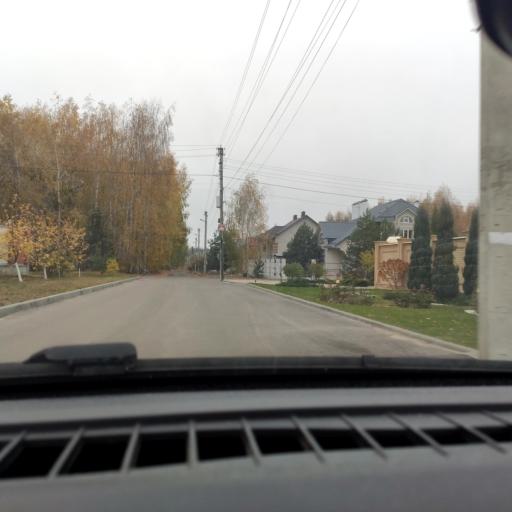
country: RU
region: Voronezj
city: Podgornoye
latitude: 51.7654
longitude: 39.1858
